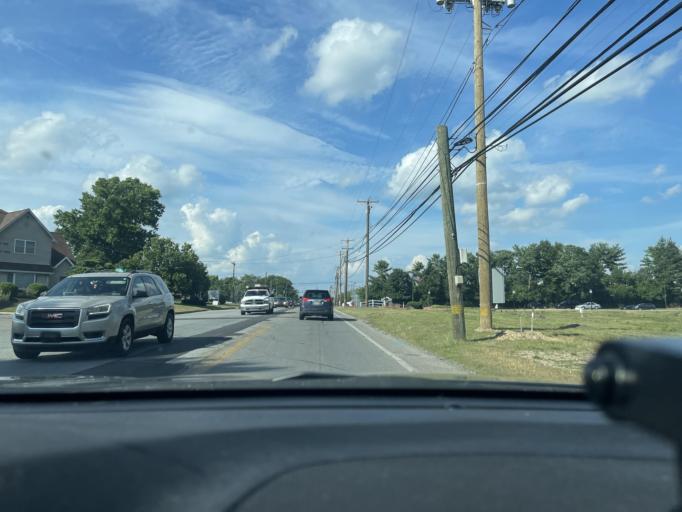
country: US
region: Pennsylvania
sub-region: Montgomery County
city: Norristown
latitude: 40.1369
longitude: -75.3174
